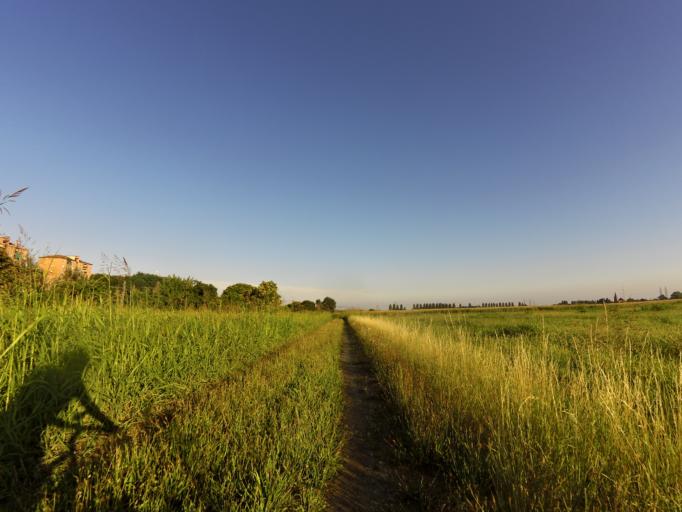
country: IT
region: Lombardy
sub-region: Citta metropolitana di Milano
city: San Giuliano Milanese
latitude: 45.3968
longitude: 9.2776
